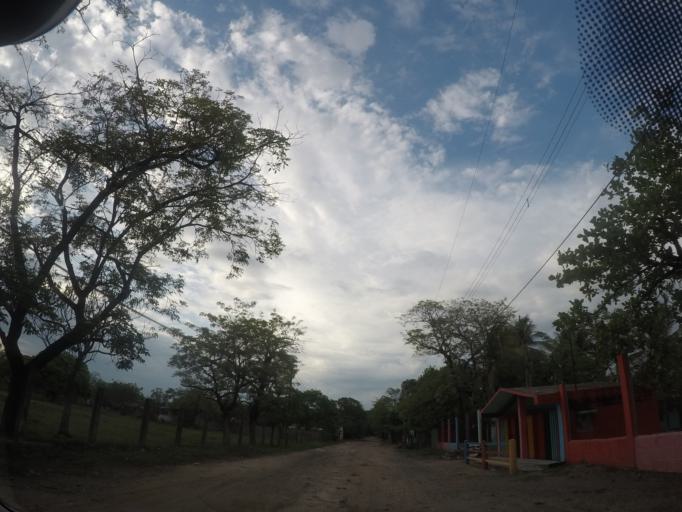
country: MX
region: Oaxaca
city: Chahuite
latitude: 16.3042
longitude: -94.1913
